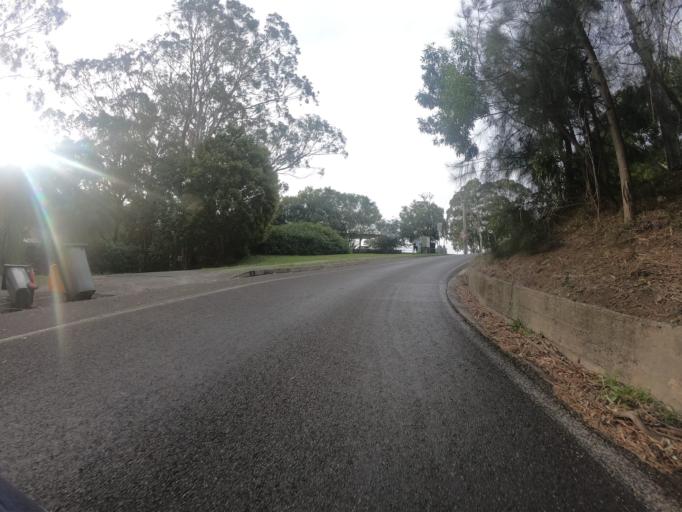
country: AU
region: New South Wales
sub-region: Wollongong
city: Mount Keira
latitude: -34.4284
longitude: 150.8539
